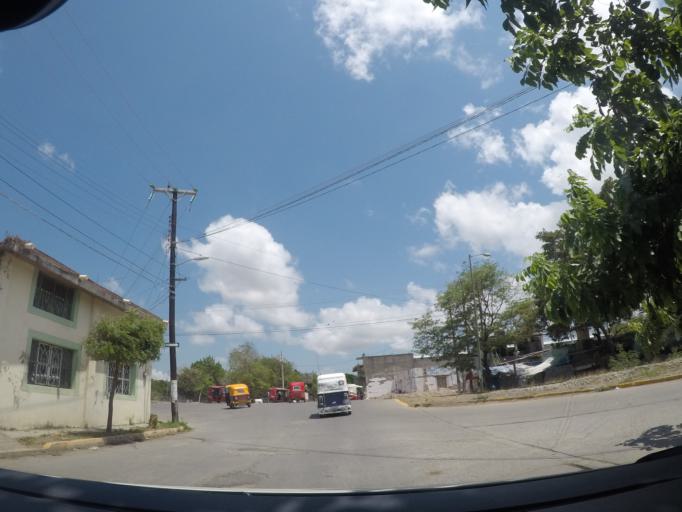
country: MX
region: Oaxaca
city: Juchitan de Zaragoza
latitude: 16.4387
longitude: -95.0162
